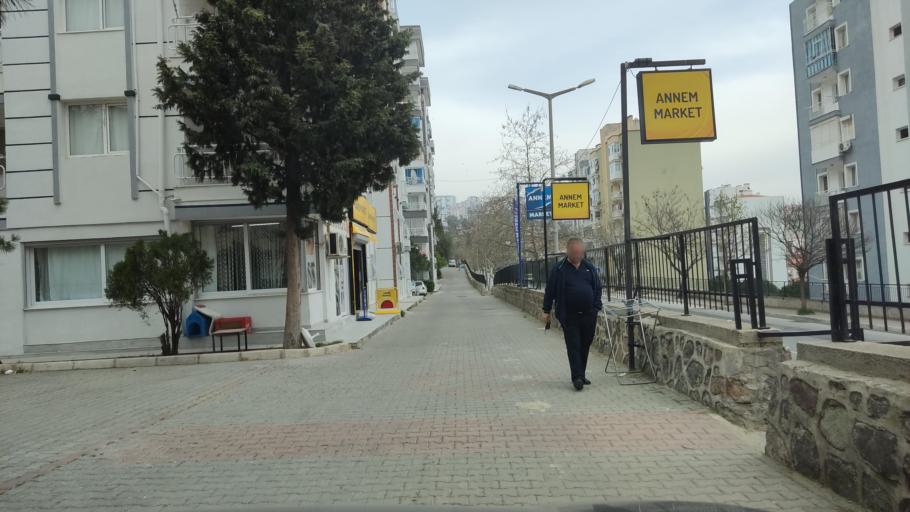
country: TR
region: Izmir
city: Karsiyaka
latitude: 38.5038
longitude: 27.0729
